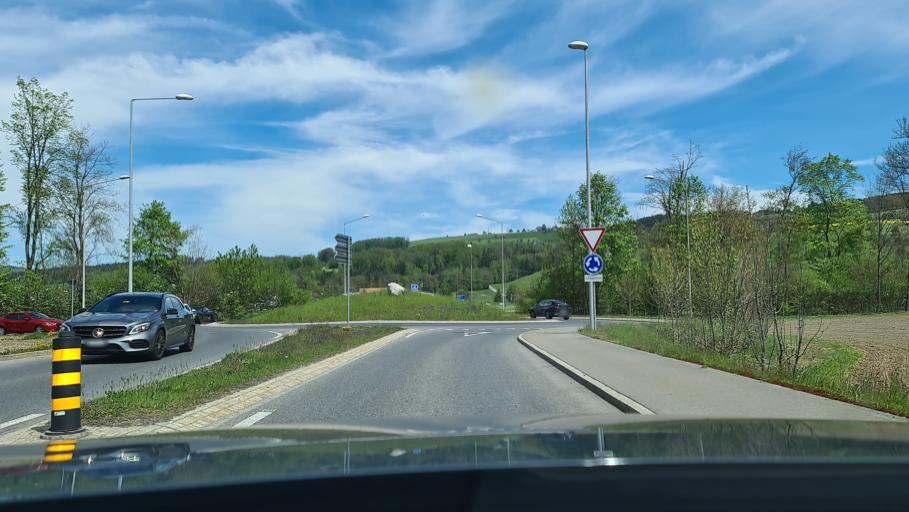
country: CH
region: Lucerne
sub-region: Sursee District
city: Sursee
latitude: 47.1843
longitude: 8.1122
